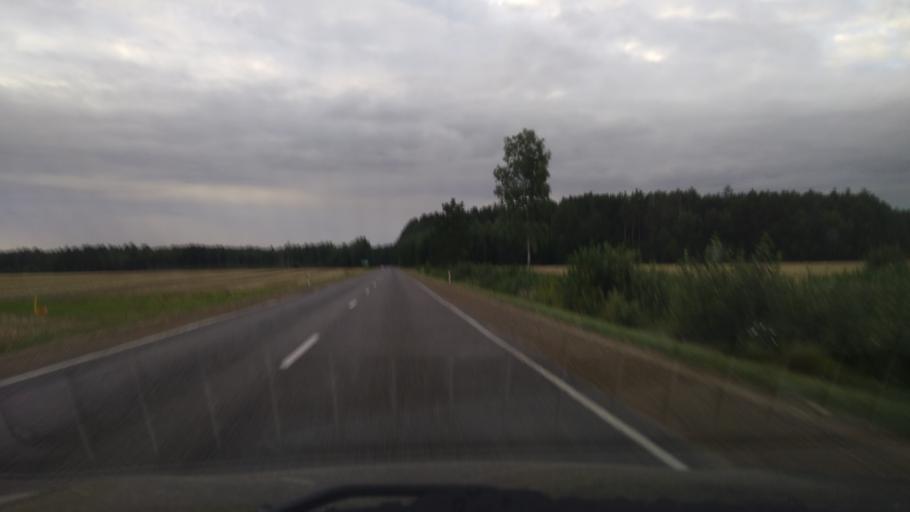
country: BY
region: Brest
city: Byaroza
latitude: 52.4009
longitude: 25.0034
